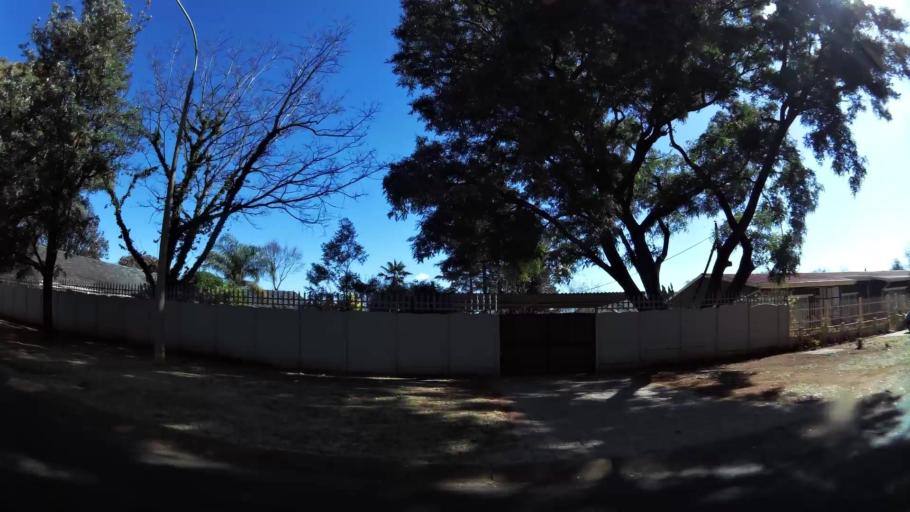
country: ZA
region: Gauteng
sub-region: West Rand District Municipality
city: Carletonville
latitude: -26.3500
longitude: 27.3874
